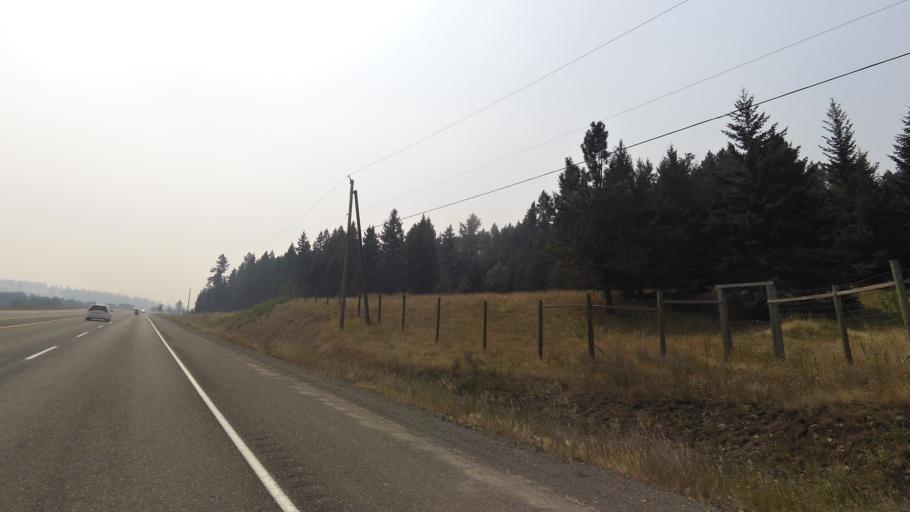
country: CA
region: British Columbia
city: Merritt
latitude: 50.0356
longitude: -120.6312
